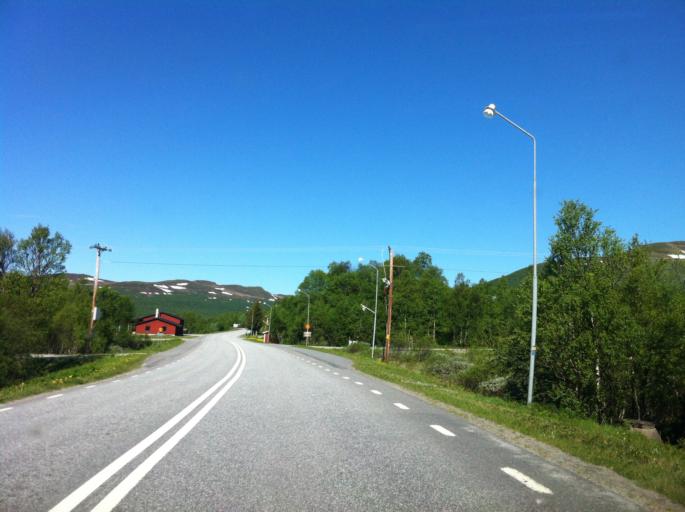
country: NO
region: Sor-Trondelag
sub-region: Tydal
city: Aas
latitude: 62.5476
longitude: 12.3218
